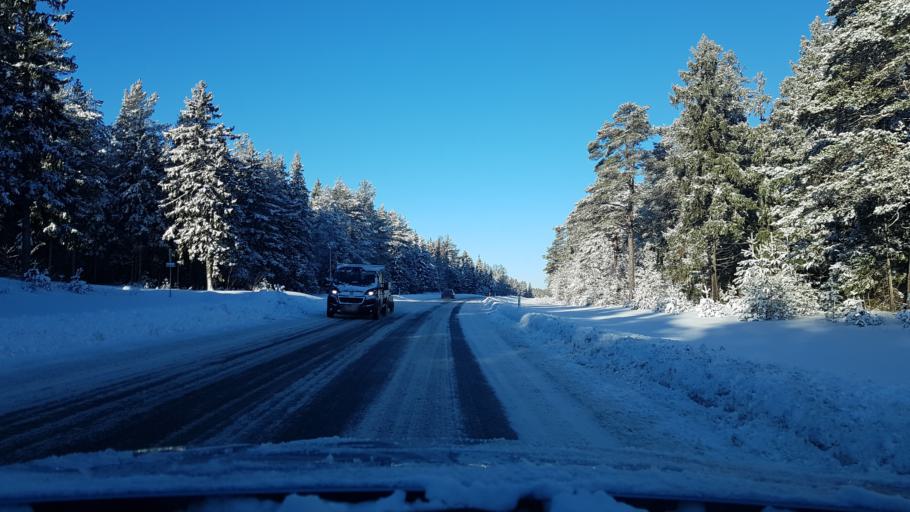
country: EE
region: Hiiumaa
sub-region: Kaerdla linn
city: Kardla
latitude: 58.9652
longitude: 22.8362
